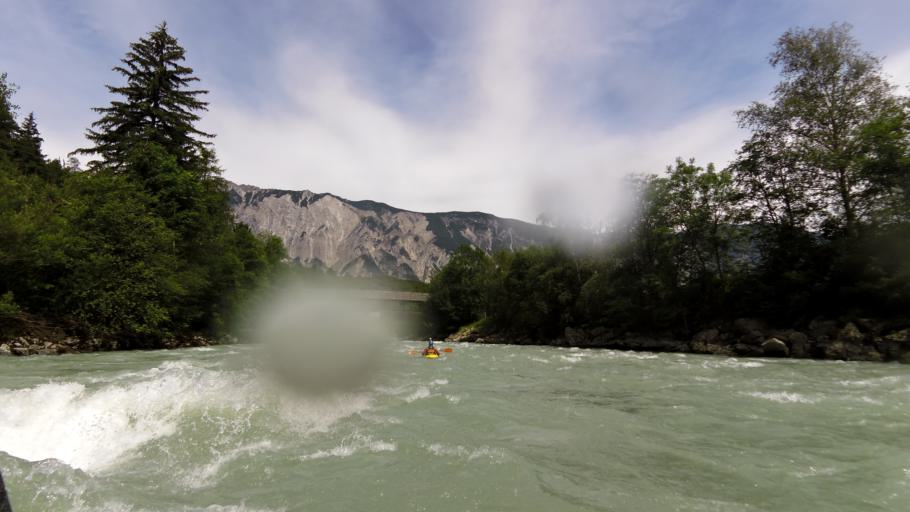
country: AT
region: Tyrol
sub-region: Politischer Bezirk Imst
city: Sautens
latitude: 47.2171
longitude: 10.8586
